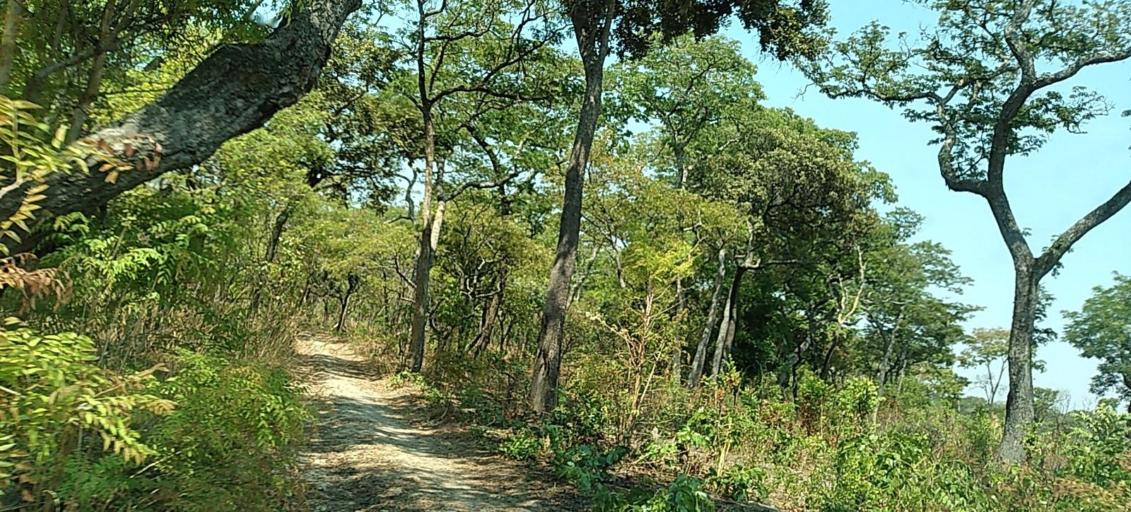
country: ZM
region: Copperbelt
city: Mpongwe
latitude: -13.7954
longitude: 28.0853
